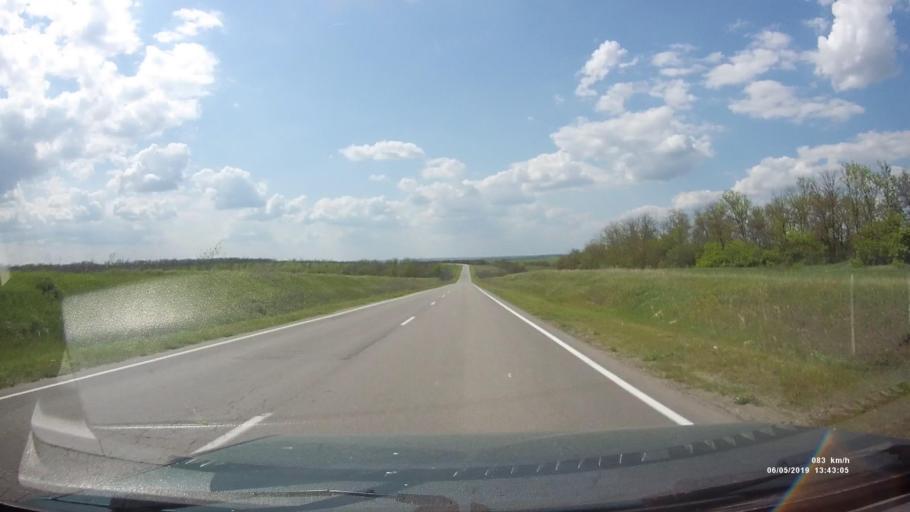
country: RU
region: Rostov
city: Semikarakorsk
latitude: 47.6598
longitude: 40.6454
